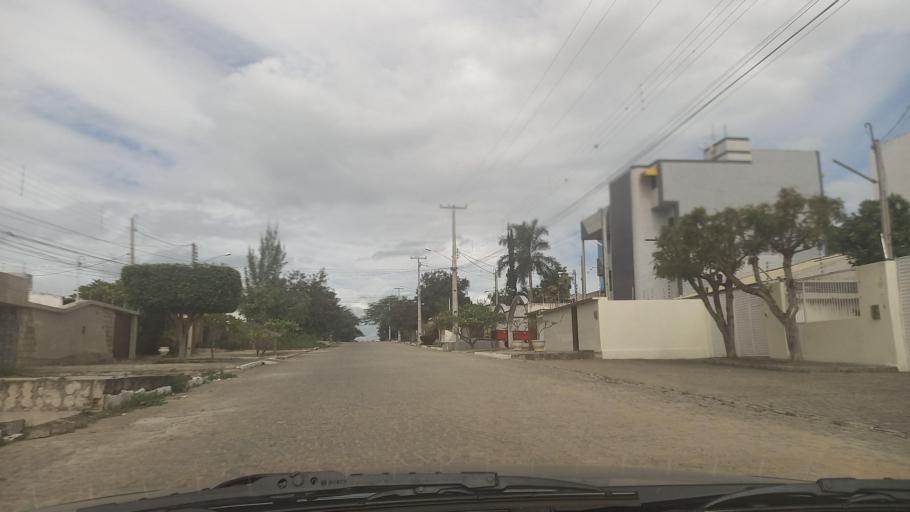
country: BR
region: Pernambuco
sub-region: Caruaru
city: Caruaru
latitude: -8.2947
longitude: -35.9911
